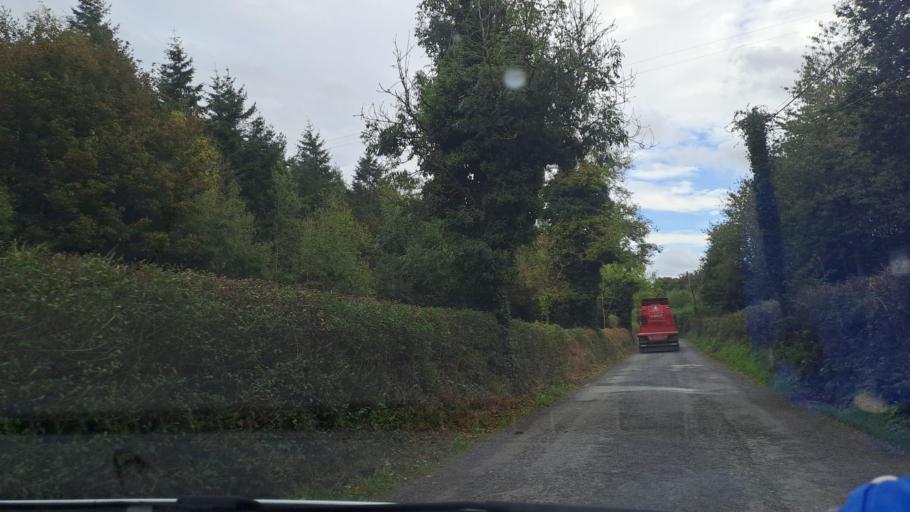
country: IE
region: Ulster
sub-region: An Cabhan
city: Kingscourt
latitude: 53.9415
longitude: -6.7931
